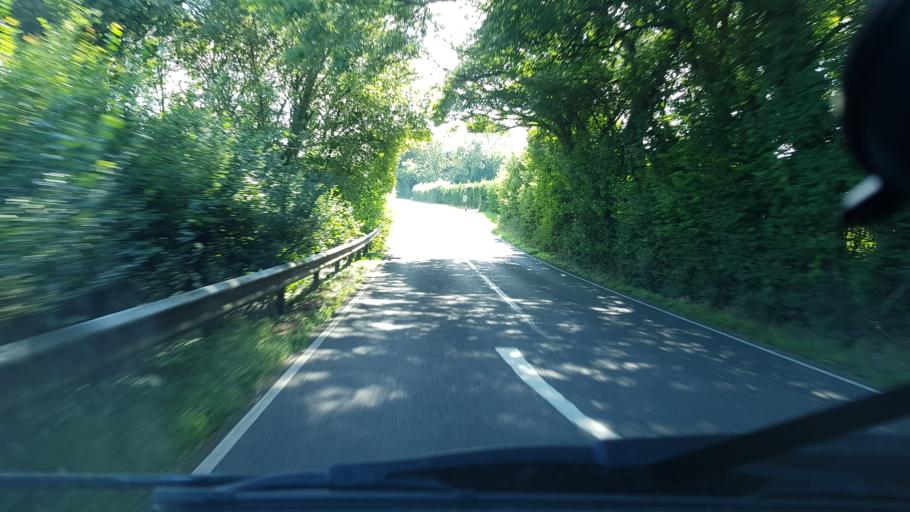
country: GB
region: England
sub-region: Surrey
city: Ockley
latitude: 51.0972
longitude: -0.3813
